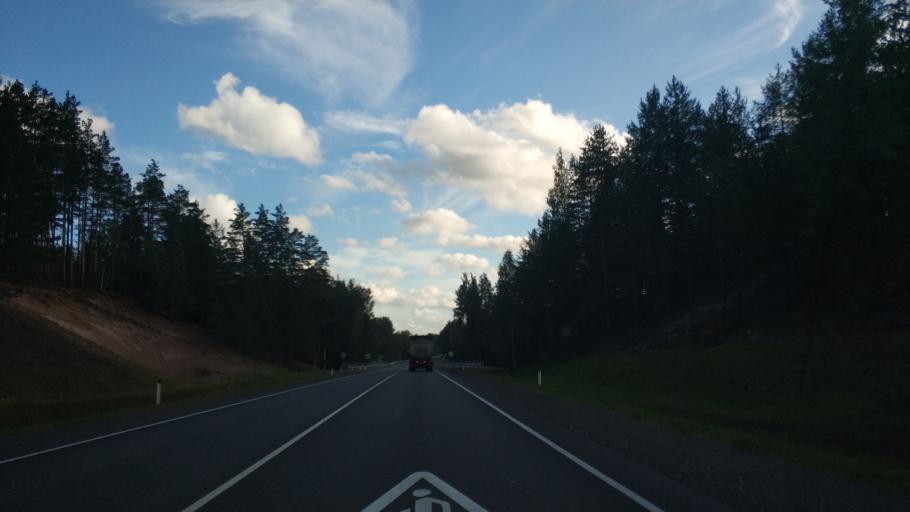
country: RU
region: Leningrad
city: Priozersk
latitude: 60.8677
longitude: 30.1601
